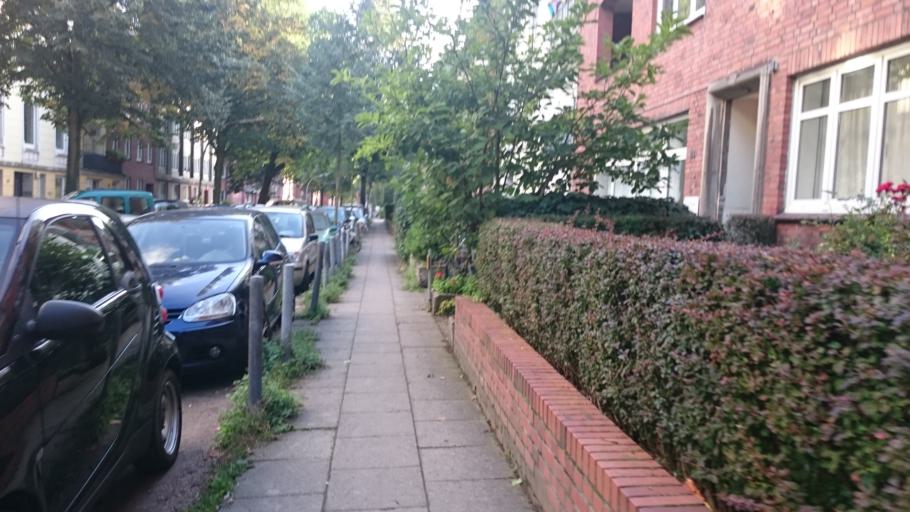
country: DE
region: Hamburg
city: Hamburg-Nord
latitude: 53.5817
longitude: 9.9637
